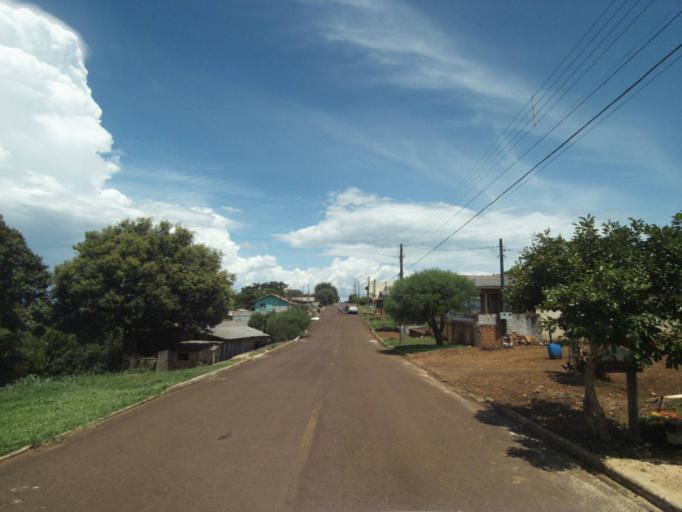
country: BR
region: Parana
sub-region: Guaraniacu
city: Guaraniacu
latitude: -25.0895
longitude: -52.8761
